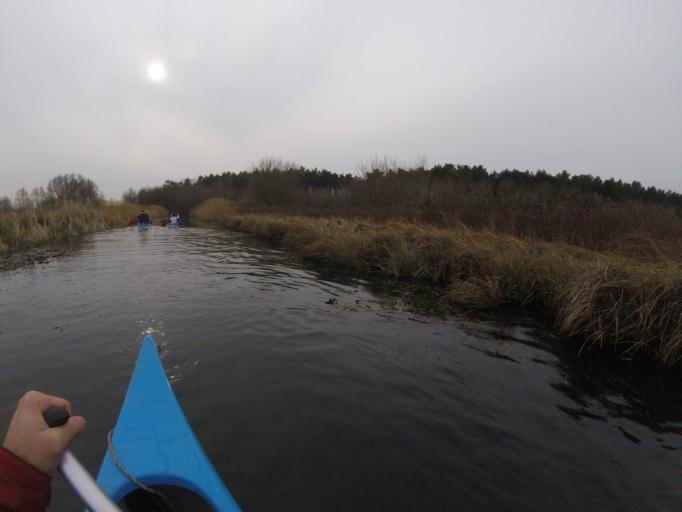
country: HU
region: Zala
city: Heviz
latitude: 46.7620
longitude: 17.2048
